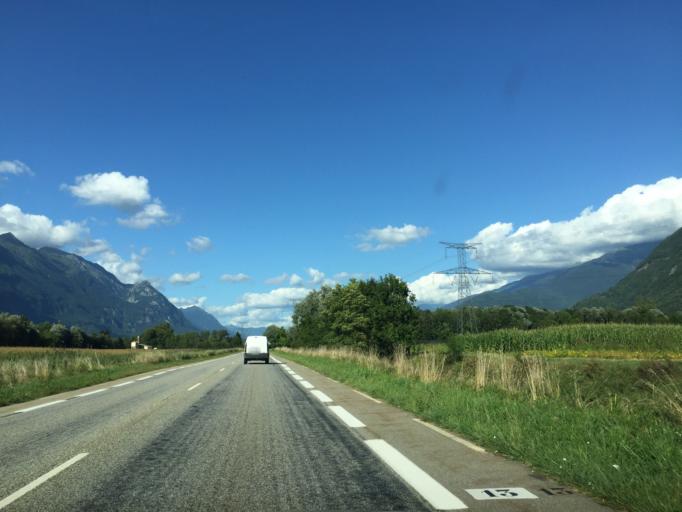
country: FR
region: Rhone-Alpes
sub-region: Departement de la Savoie
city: Coise-Saint-Jean-Pied-Gauthier
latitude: 45.5295
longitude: 6.1934
